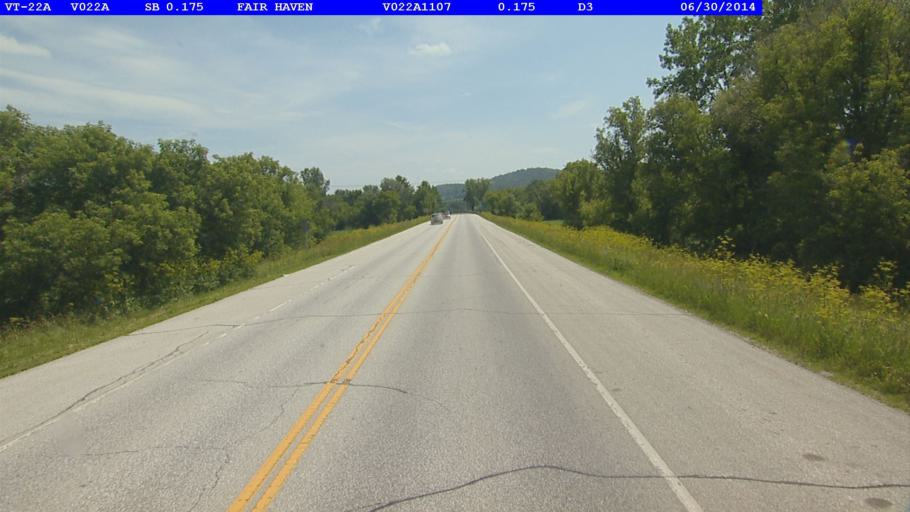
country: US
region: Vermont
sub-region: Rutland County
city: Fair Haven
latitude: 43.5699
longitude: -73.2635
